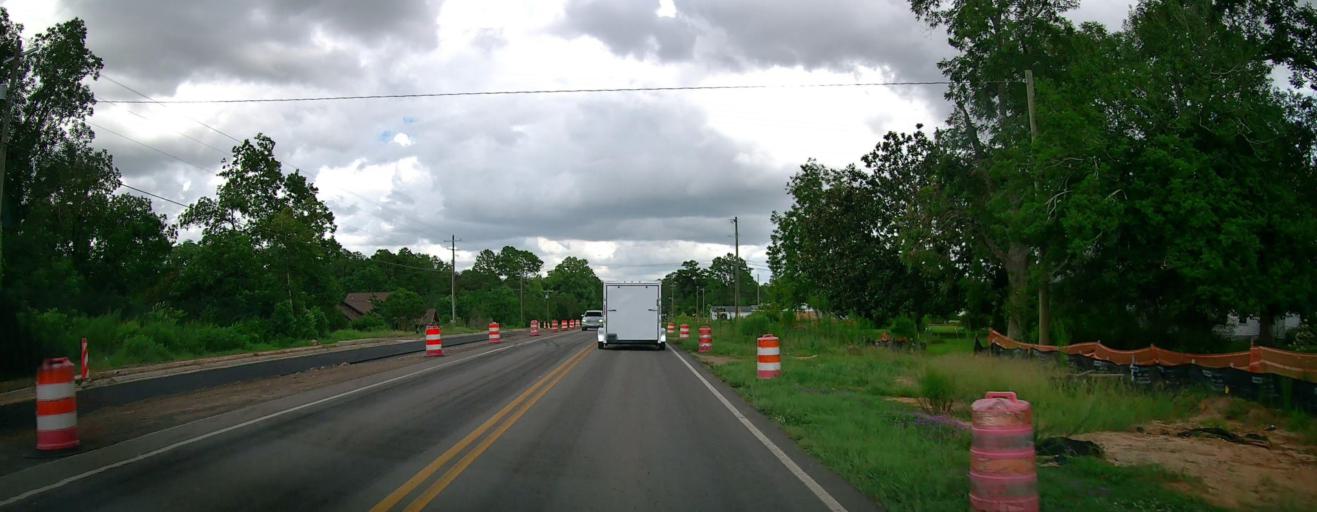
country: US
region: Georgia
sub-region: Coffee County
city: Douglas
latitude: 31.5176
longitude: -82.8837
